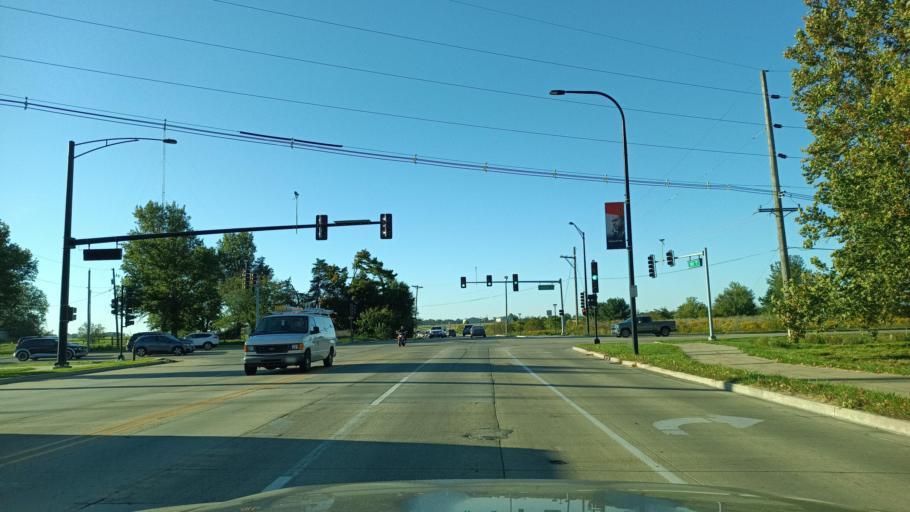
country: US
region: Illinois
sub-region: Champaign County
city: Savoy
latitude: 40.0840
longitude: -88.2383
